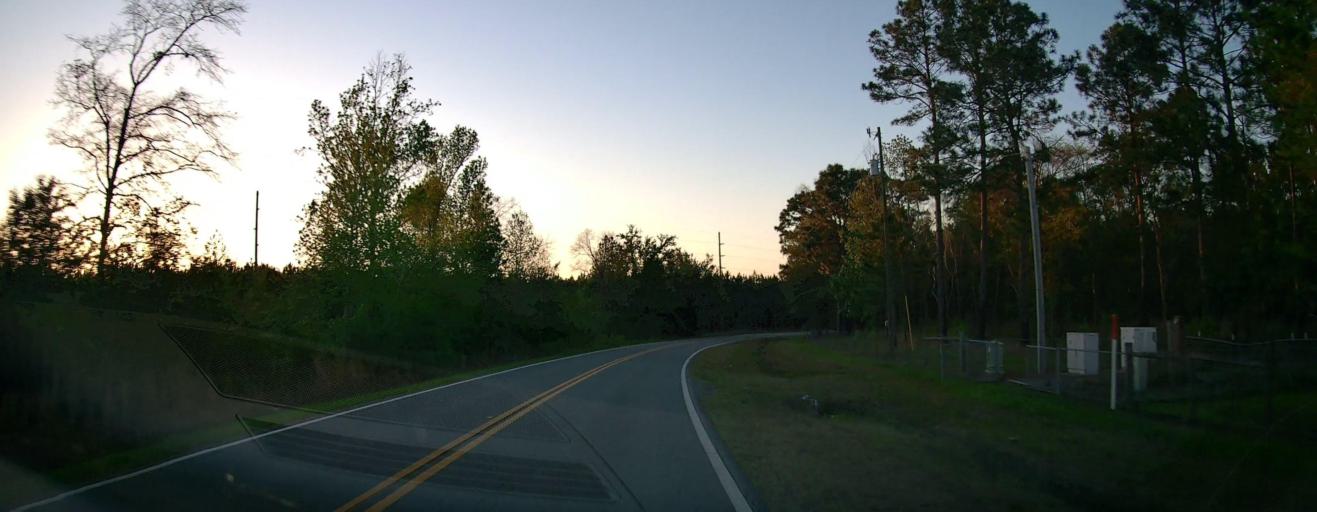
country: US
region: Georgia
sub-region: Ben Hill County
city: Fitzgerald
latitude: 31.7578
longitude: -83.3539
